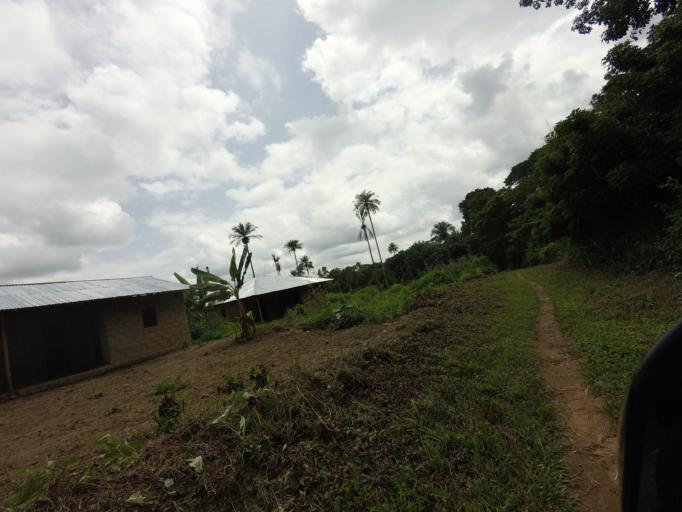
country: SL
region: Eastern Province
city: Tombodu
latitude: 8.1791
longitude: -10.6042
